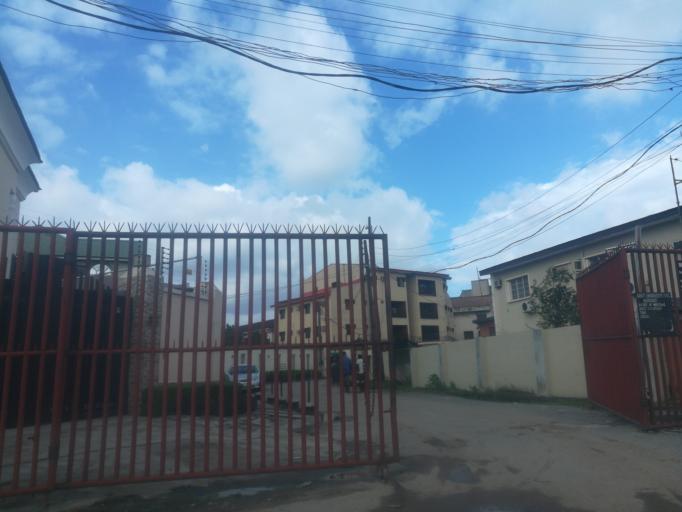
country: NG
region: Lagos
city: Somolu
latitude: 6.5476
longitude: 3.3750
